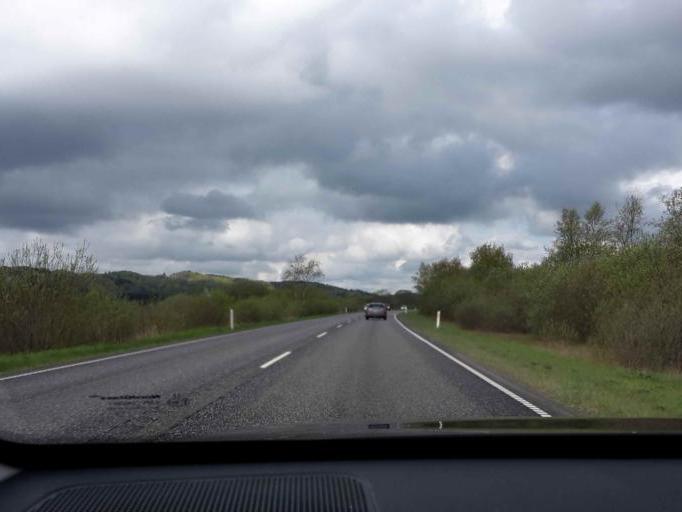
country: DK
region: South Denmark
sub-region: Vejle Kommune
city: Vejle
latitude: 55.7038
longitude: 9.5129
